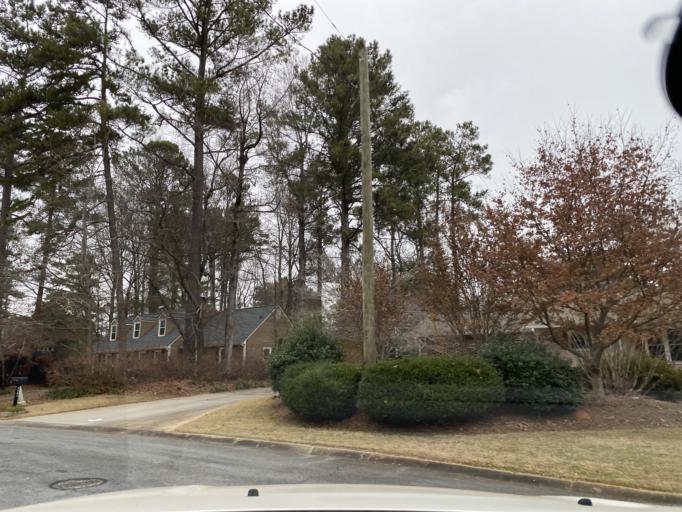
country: US
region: Georgia
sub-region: Cobb County
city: Fair Oaks
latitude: 33.9161
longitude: -84.5691
